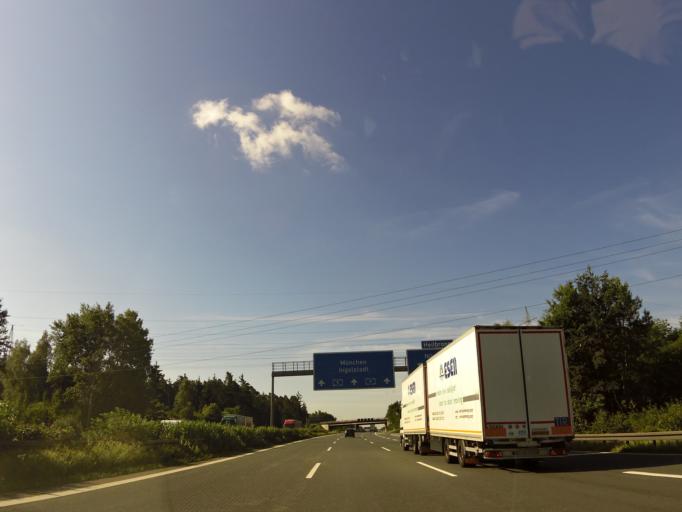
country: DE
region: Bavaria
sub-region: Regierungsbezirk Mittelfranken
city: Feucht
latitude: 49.3529
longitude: 11.2034
